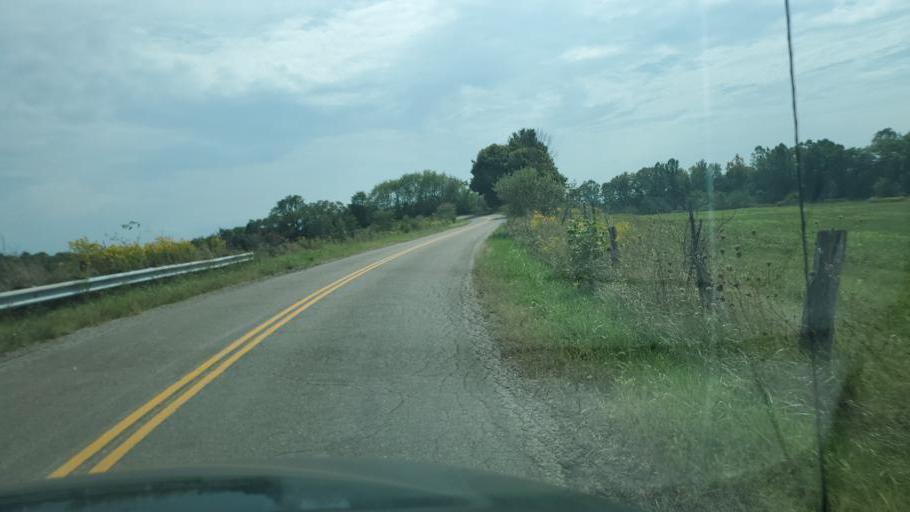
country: US
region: Ohio
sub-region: Muskingum County
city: Zanesville
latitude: 39.9411
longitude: -82.0820
